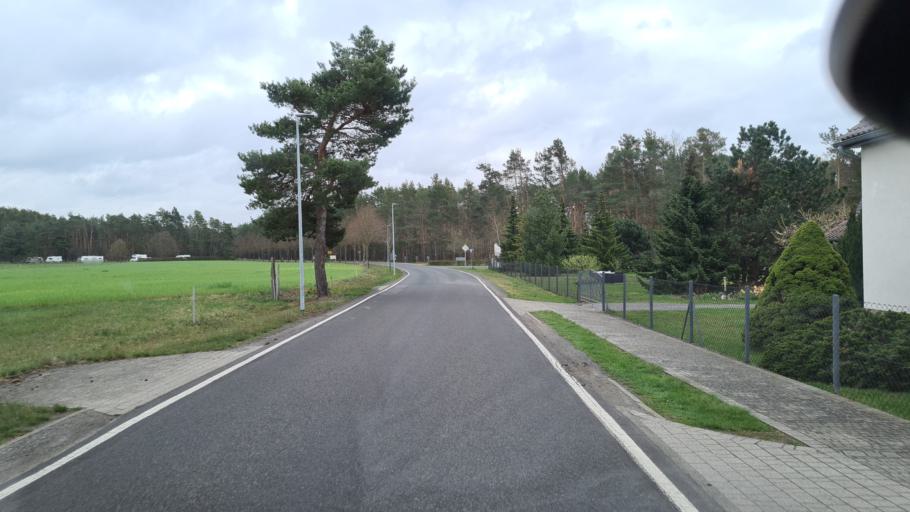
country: DE
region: Brandenburg
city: Schwarzbach
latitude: 51.4504
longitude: 13.9405
